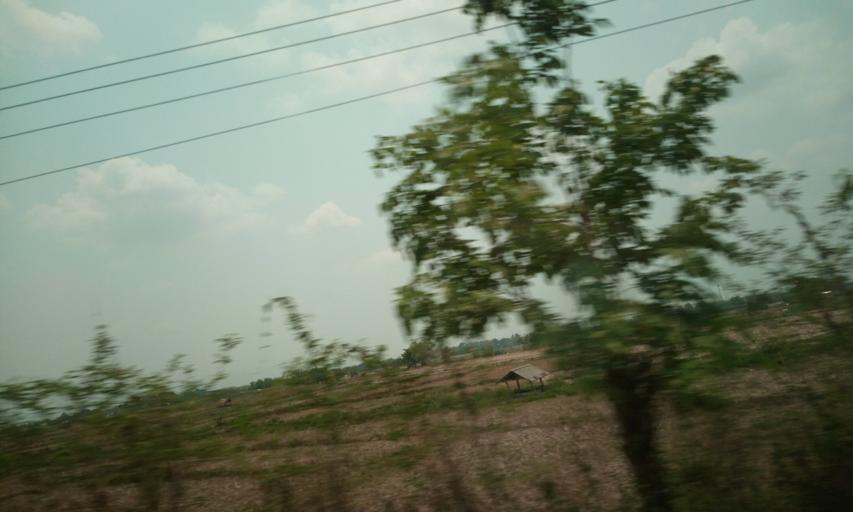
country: TH
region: Phayao
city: Phu Sang
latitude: 19.6078
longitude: 100.2946
